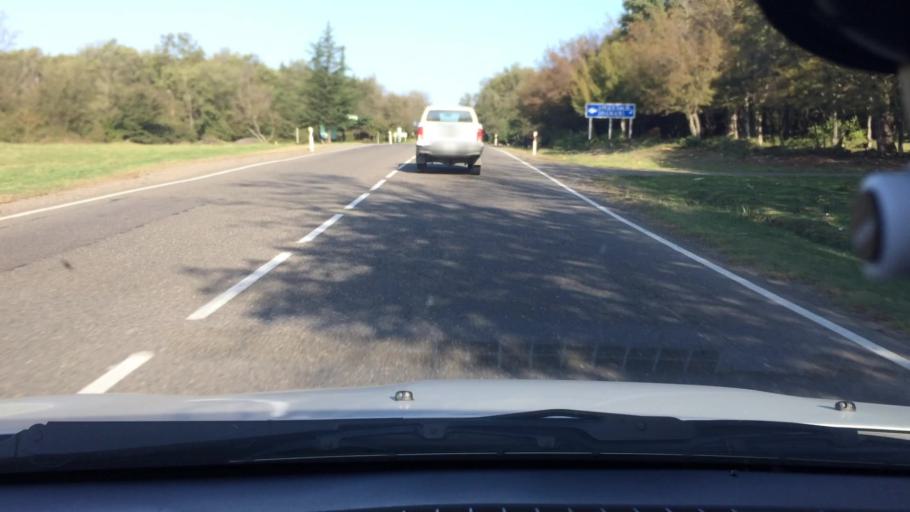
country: GE
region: Imereti
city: Kutaisi
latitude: 42.2322
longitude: 42.7756
